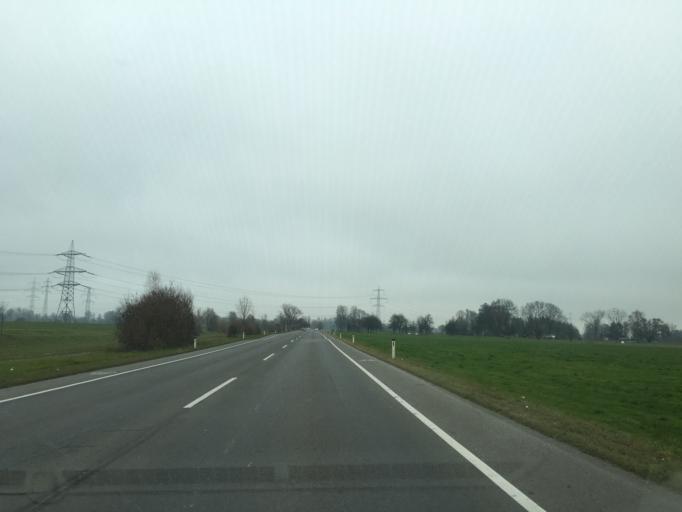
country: AT
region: Vorarlberg
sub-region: Politischer Bezirk Dornbirn
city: Hohenems
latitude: 47.3823
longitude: 9.6811
